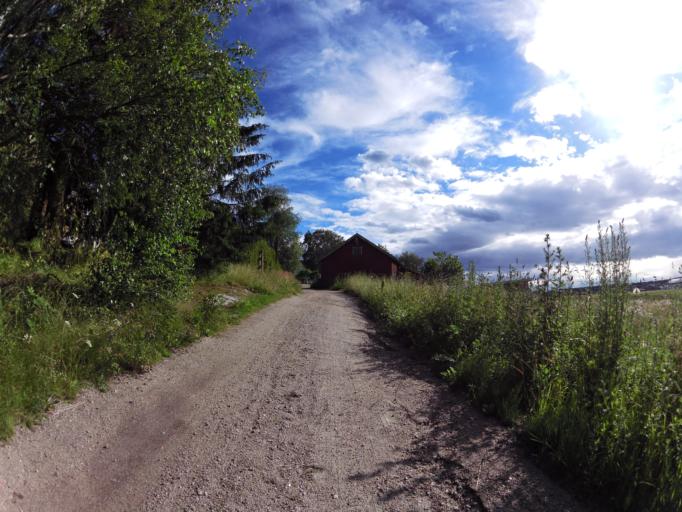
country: NO
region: Ostfold
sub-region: Fredrikstad
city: Fredrikstad
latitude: 59.2525
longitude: 11.0114
